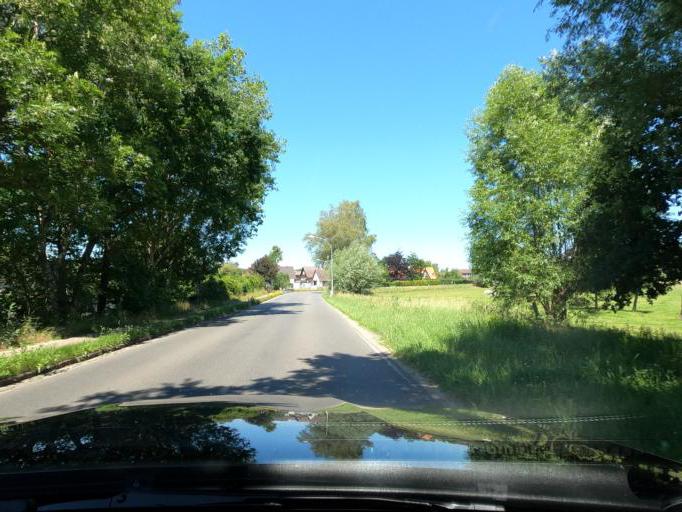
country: DE
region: Lower Saxony
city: Wienhausen
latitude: 52.5905
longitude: 10.2078
